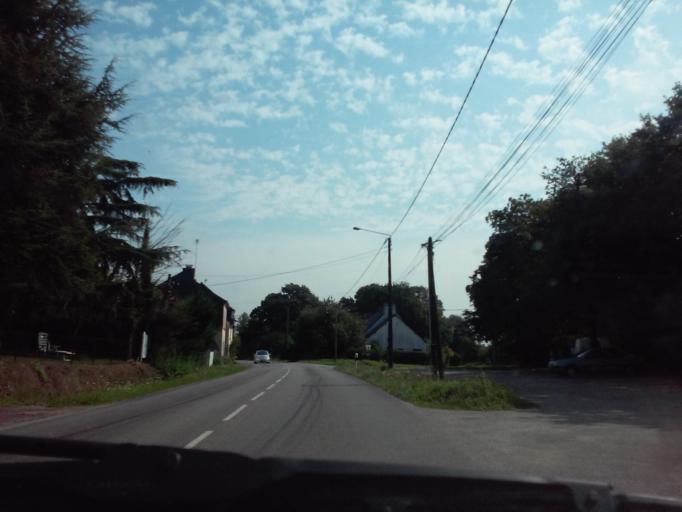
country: FR
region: Brittany
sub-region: Departement du Morbihan
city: Ploermel
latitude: 47.9250
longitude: -2.3480
